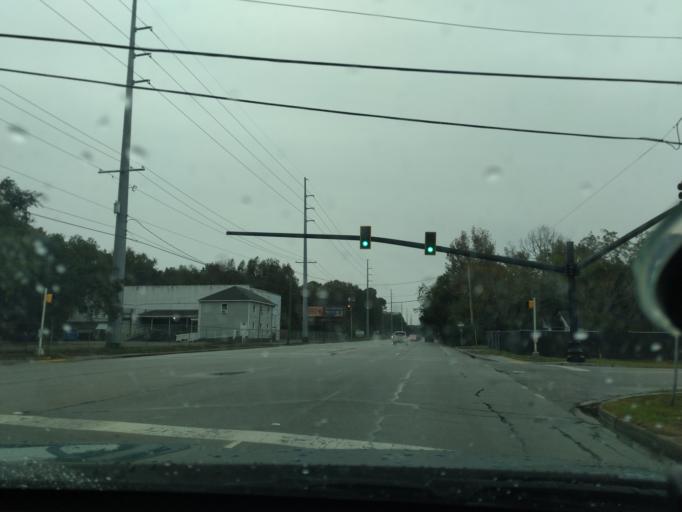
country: US
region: South Carolina
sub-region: Charleston County
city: Folly Beach
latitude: 32.7015
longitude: -79.9667
